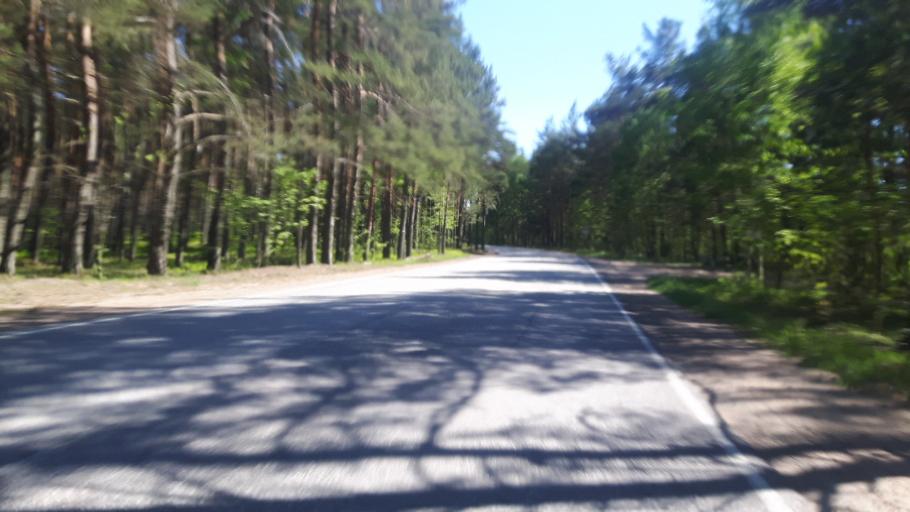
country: RU
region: Leningrad
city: Glebychevo
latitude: 60.2903
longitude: 28.8704
